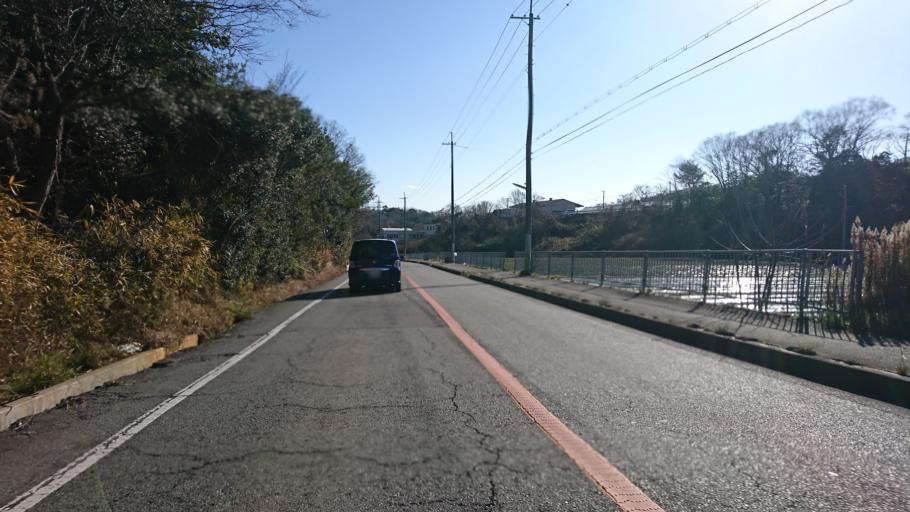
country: JP
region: Hyogo
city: Akashi
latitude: 34.7154
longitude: 134.9700
